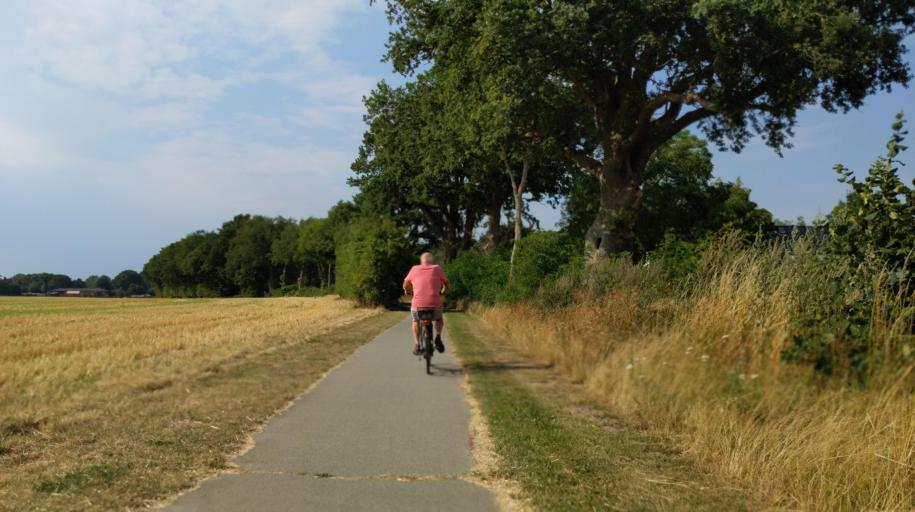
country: DE
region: Schleswig-Holstein
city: Rondeshagen
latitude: 53.7446
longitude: 10.6366
